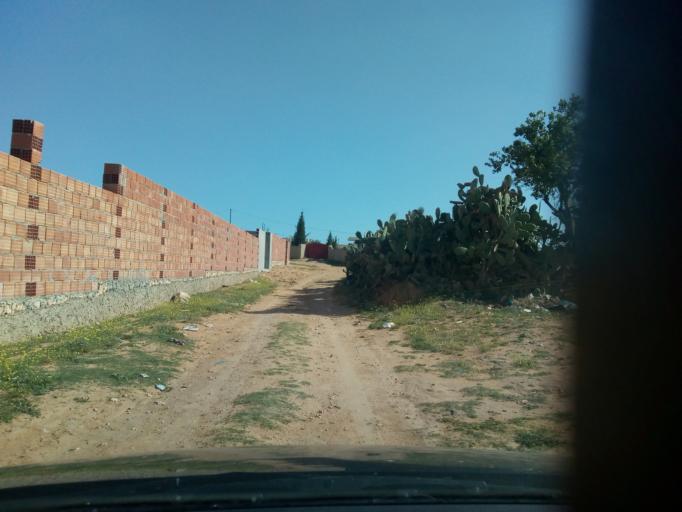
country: TN
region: Safaqis
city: Sfax
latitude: 34.7300
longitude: 10.5996
